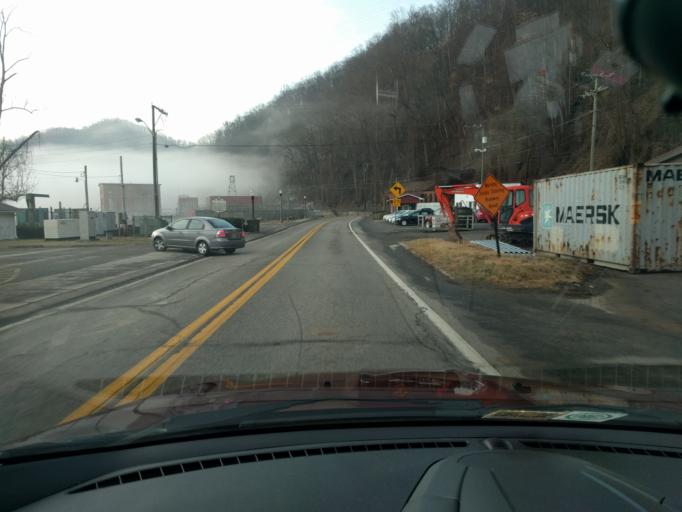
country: US
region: West Virginia
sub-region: Fayette County
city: Ansted
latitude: 38.1498
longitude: -81.2150
